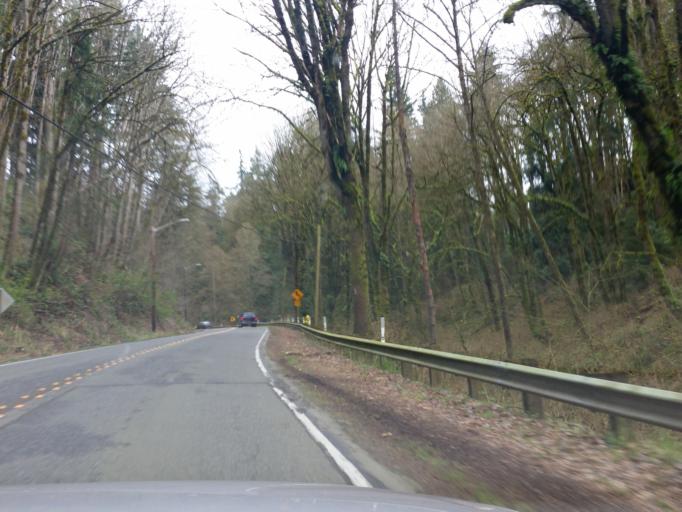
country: US
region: Washington
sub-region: King County
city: Woodinville
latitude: 47.7516
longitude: -122.1467
